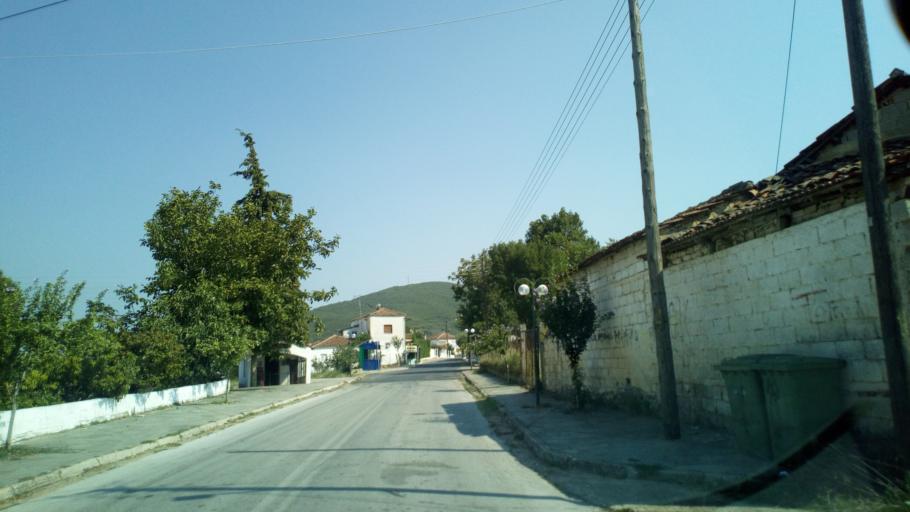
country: GR
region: Central Macedonia
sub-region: Nomos Chalkidikis
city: Galatista
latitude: 40.5567
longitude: 23.3007
